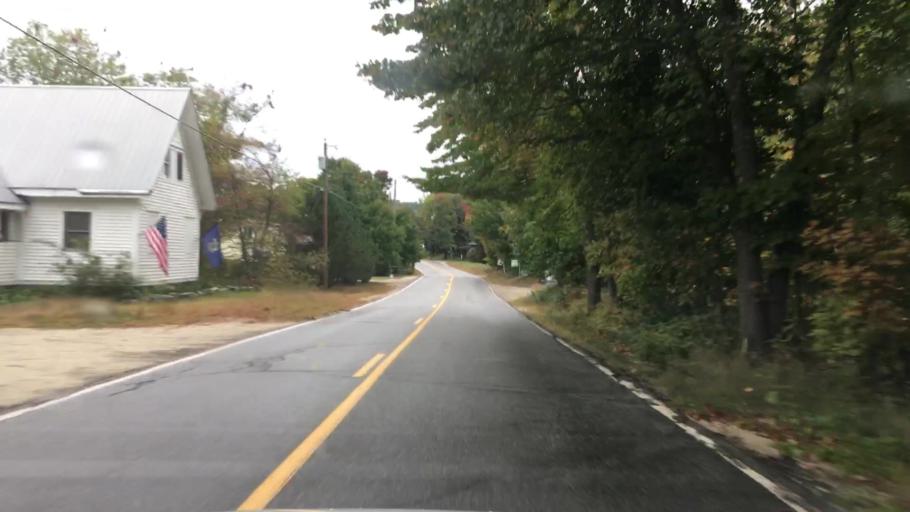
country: US
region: Maine
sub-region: Cumberland County
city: Raymond
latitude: 43.9822
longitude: -70.4735
